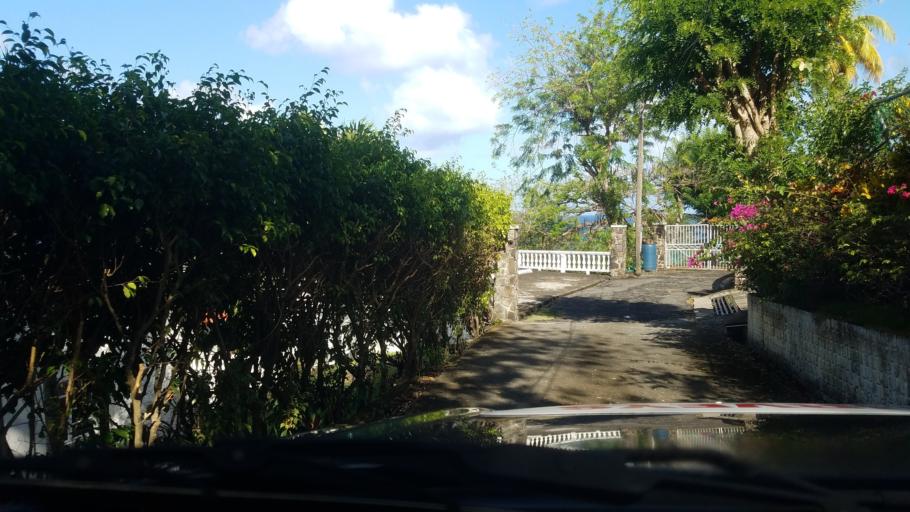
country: LC
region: Castries Quarter
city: Castries
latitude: 14.0217
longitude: -61.0043
